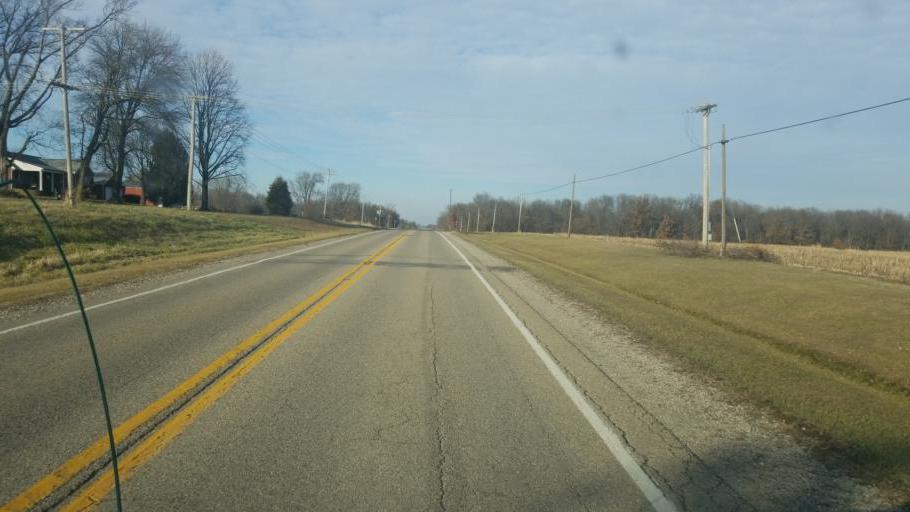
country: US
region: Illinois
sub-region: Lawrence County
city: Lawrenceville
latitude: 38.6583
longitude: -87.6942
